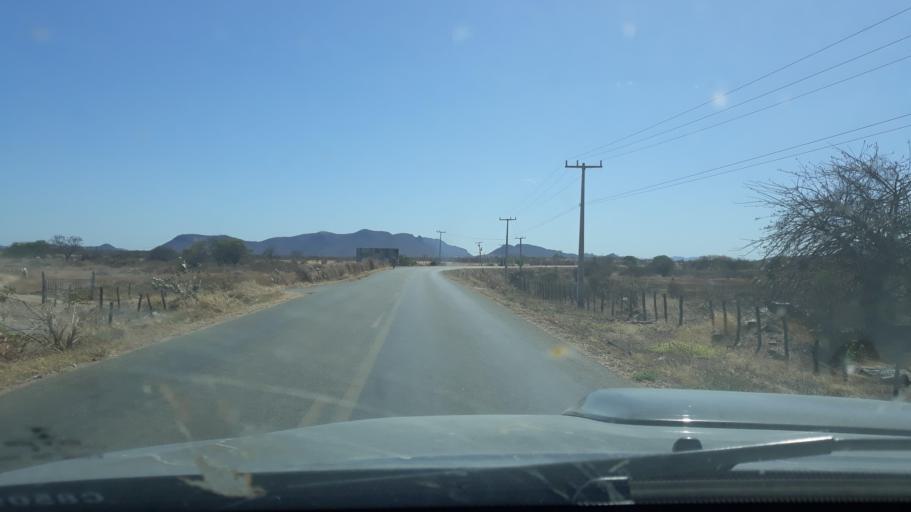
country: BR
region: Bahia
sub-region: Guanambi
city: Guanambi
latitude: -14.1911
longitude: -42.7973
